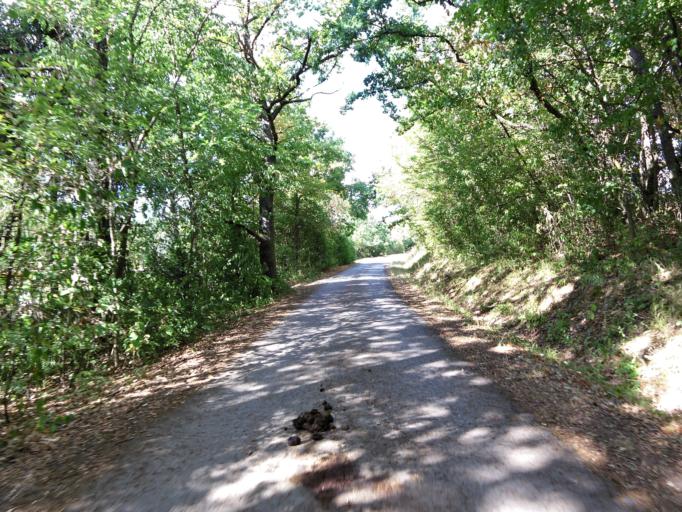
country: DE
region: Bavaria
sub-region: Regierungsbezirk Unterfranken
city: Veitshochheim
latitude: 49.8457
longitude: 9.8767
